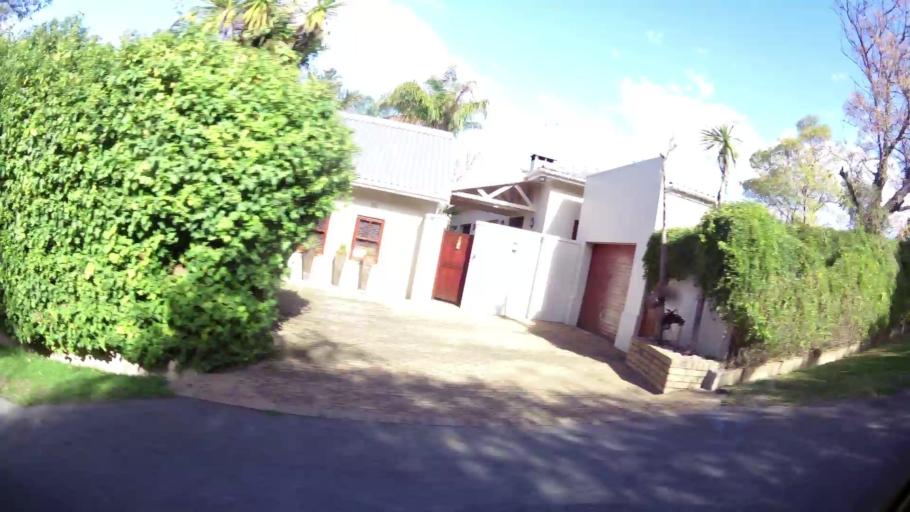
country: ZA
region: Western Cape
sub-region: Overberg District Municipality
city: Swellendam
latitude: -34.0172
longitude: 20.4433
